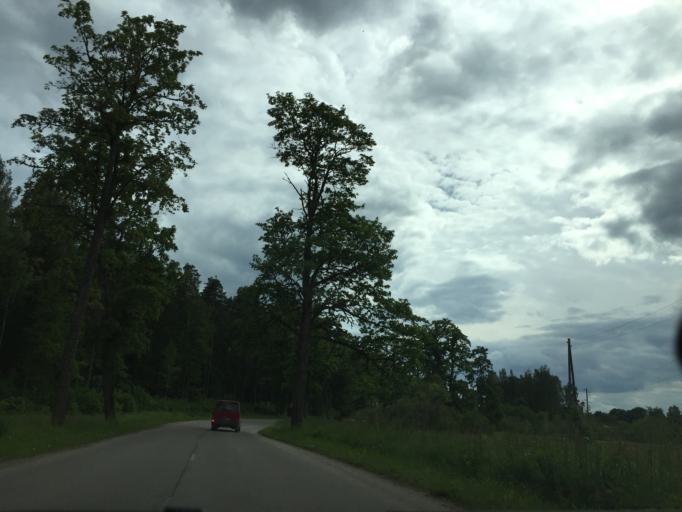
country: LV
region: Apes Novads
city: Ape
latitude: 57.5112
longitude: 26.4037
